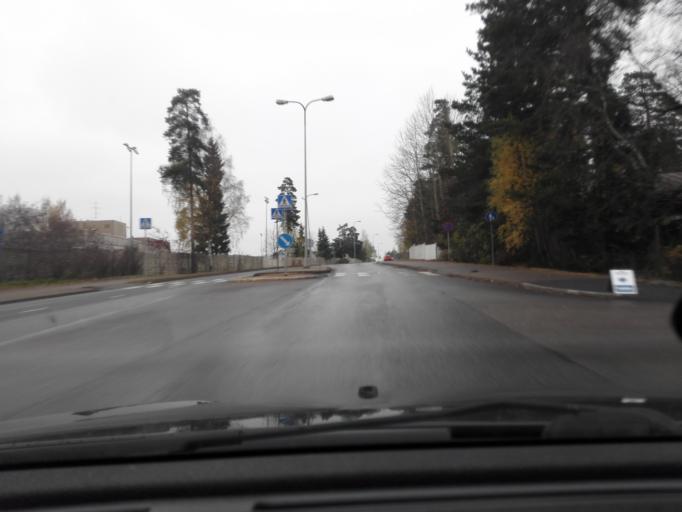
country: FI
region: Uusimaa
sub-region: Helsinki
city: Vantaa
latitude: 60.2828
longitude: 25.0795
